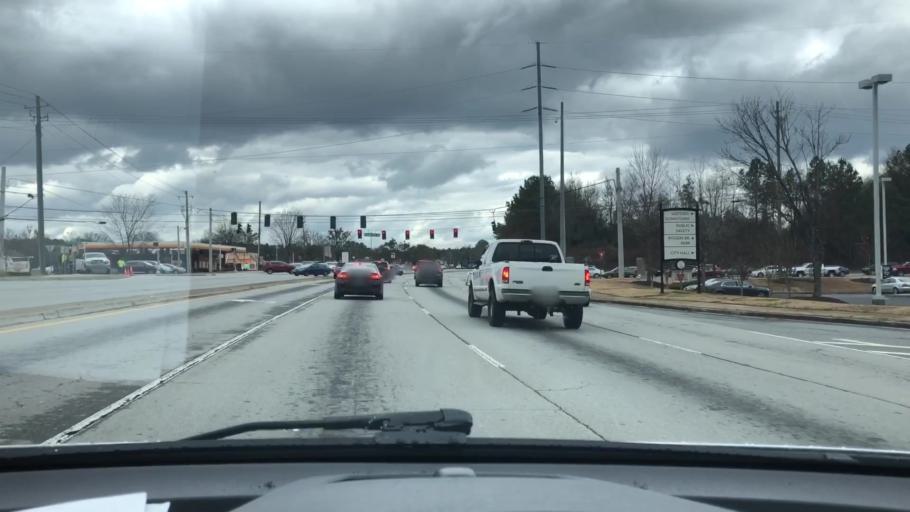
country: US
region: Georgia
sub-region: Gwinnett County
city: Duluth
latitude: 34.0036
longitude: -84.1699
